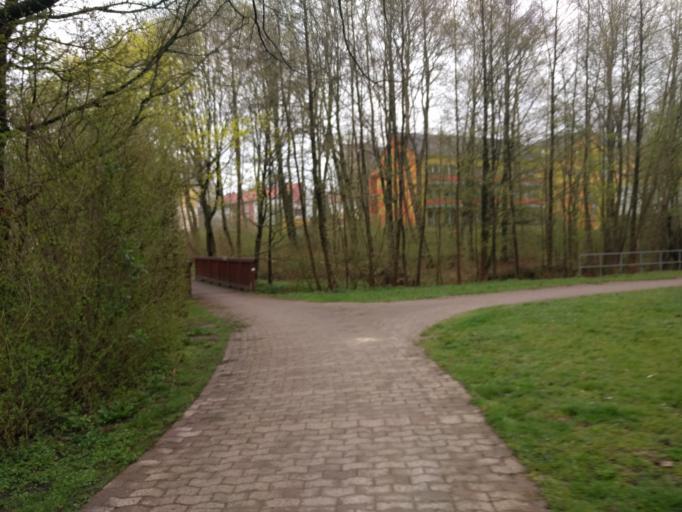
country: DE
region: North Rhine-Westphalia
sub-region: Regierungsbezirk Detmold
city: Bielefeld
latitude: 52.0505
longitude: 8.5091
